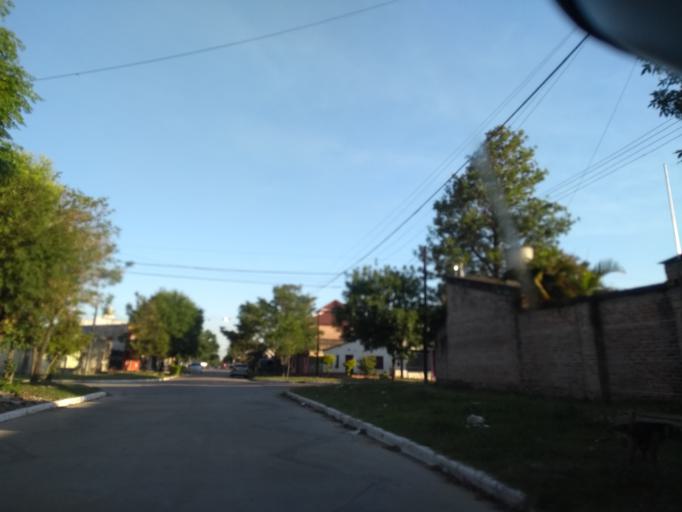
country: AR
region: Chaco
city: Barranqueras
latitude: -27.4822
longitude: -58.9463
